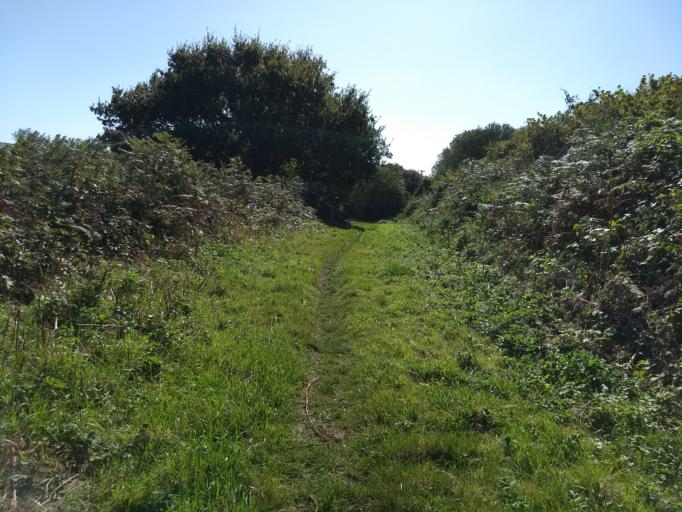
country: GB
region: England
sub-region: Isle of Wight
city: Niton
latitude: 50.6323
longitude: -1.2759
